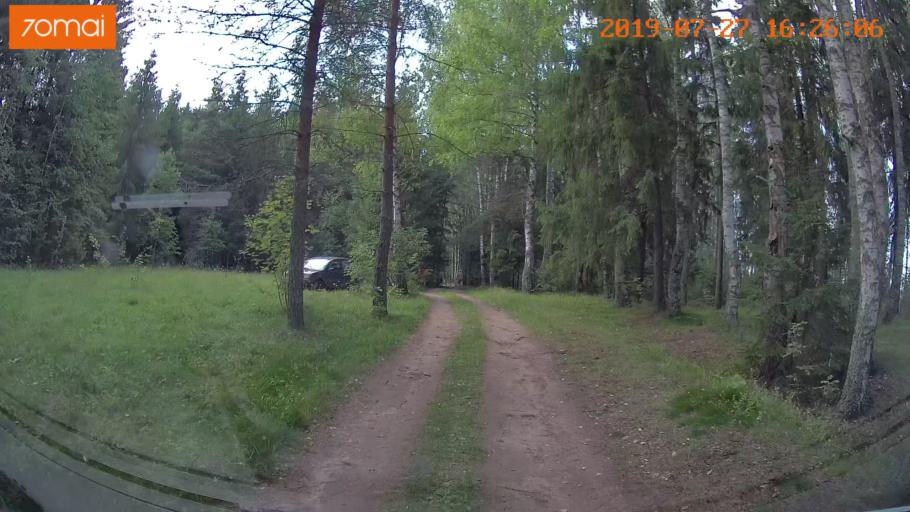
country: RU
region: Ivanovo
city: Novo-Talitsy
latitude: 57.0907
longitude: 40.8547
